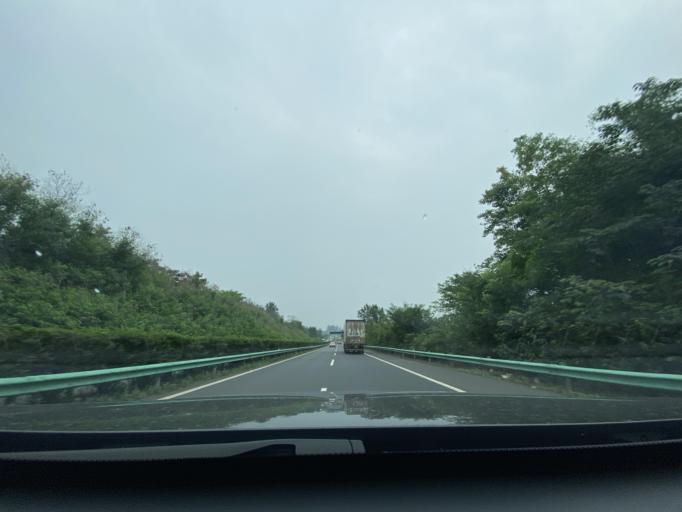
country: CN
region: Sichuan
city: Longquan
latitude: 30.3123
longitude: 104.1191
